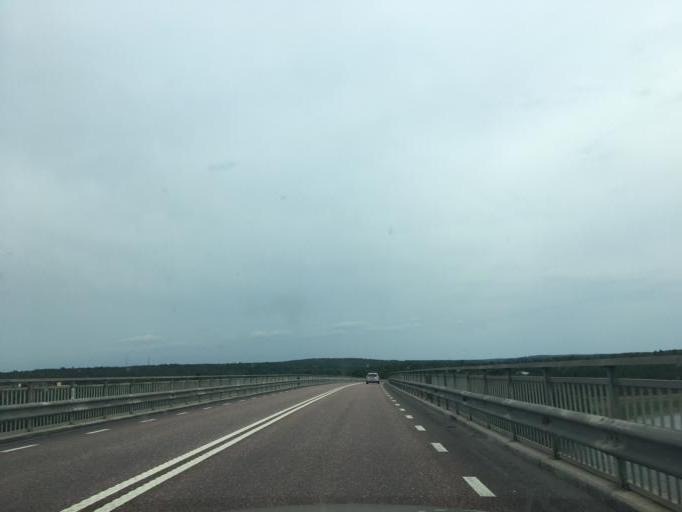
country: SE
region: Soedermanland
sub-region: Strangnas Kommun
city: Strangnas
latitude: 59.3963
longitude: 17.0092
